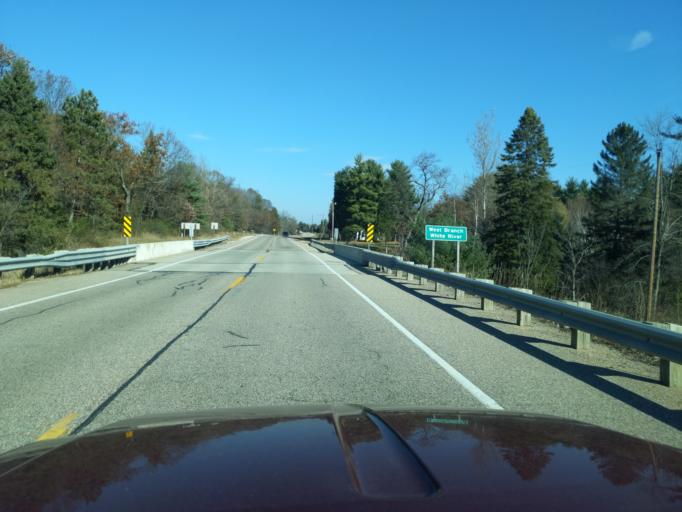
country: US
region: Wisconsin
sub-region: Waushara County
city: Wautoma
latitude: 44.0488
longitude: -89.2948
